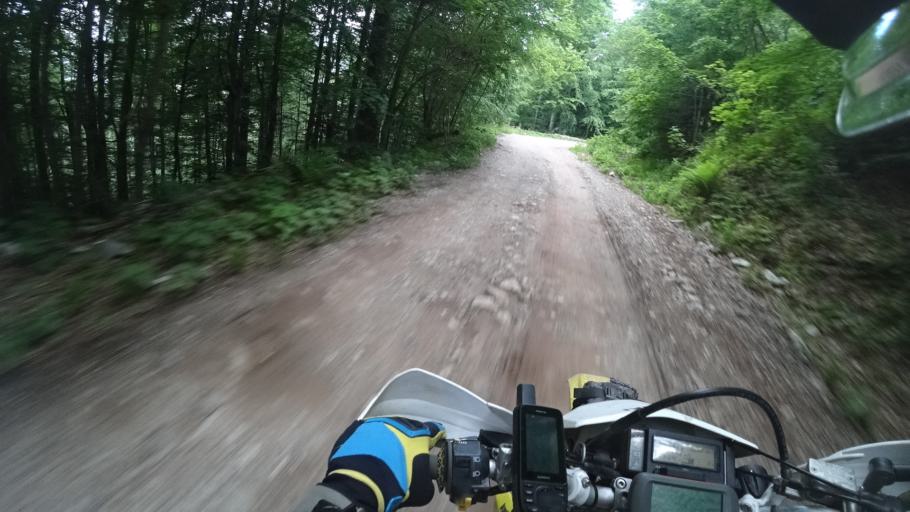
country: HR
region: Licko-Senjska
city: Gospic
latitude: 44.4662
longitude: 15.2996
